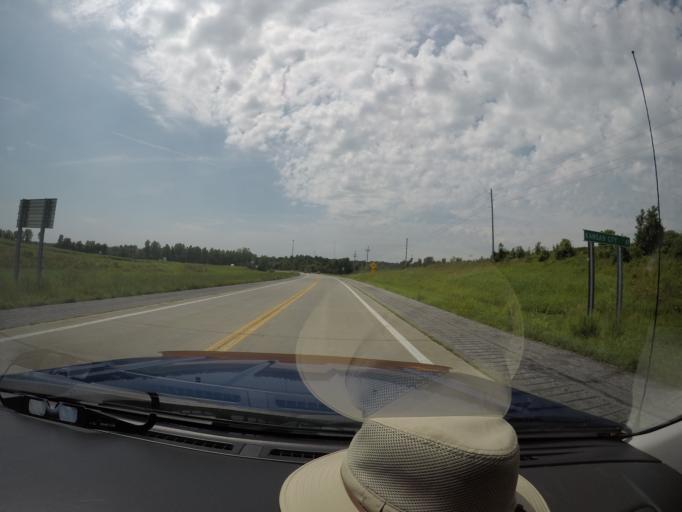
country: US
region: Missouri
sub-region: Lafayette County
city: Lexington
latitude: 39.1816
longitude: -93.8509
